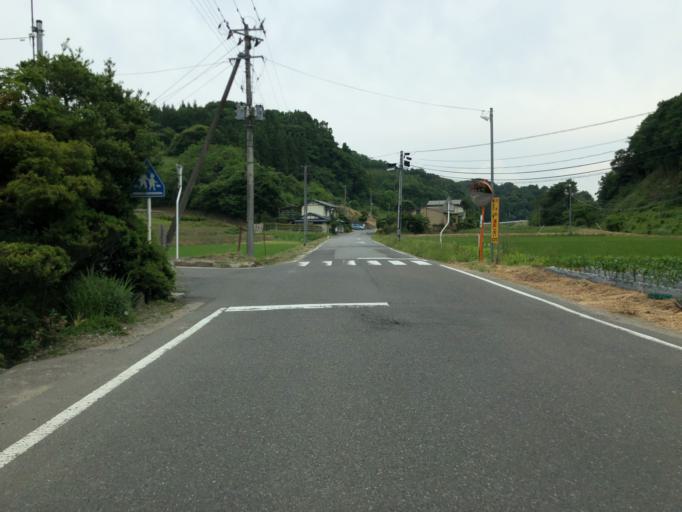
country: JP
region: Fukushima
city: Miharu
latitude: 37.4588
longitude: 140.5226
